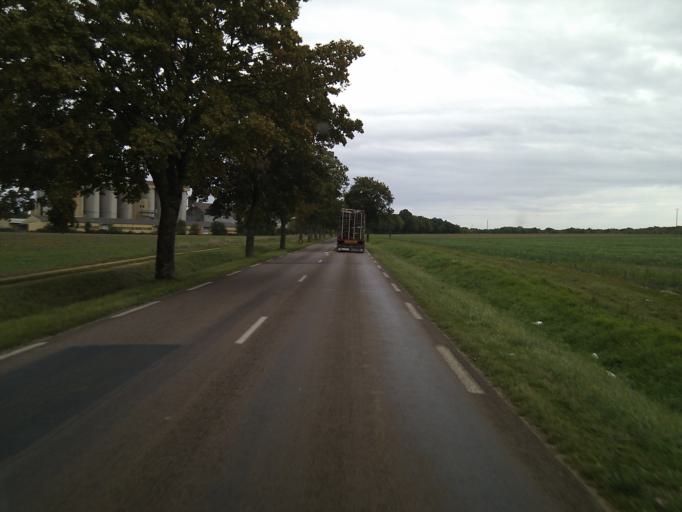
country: FR
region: Champagne-Ardenne
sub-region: Departement de la Haute-Marne
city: Chaumont
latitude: 48.1100
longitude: 5.0836
